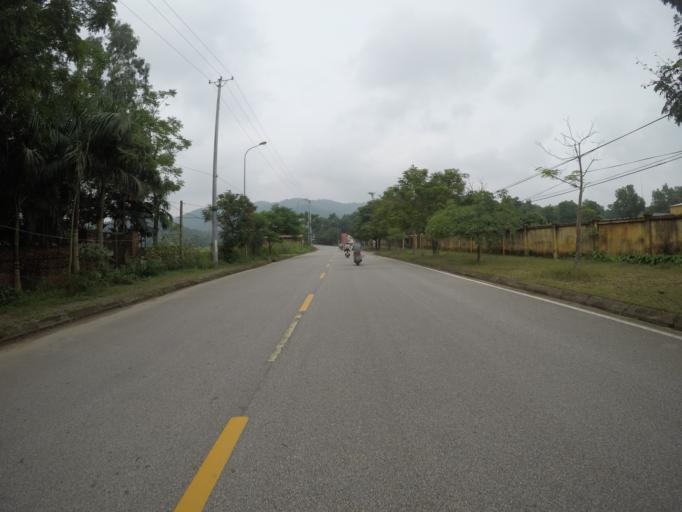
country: VN
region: Ha Noi
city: Soc Son
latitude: 21.2834
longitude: 105.8408
